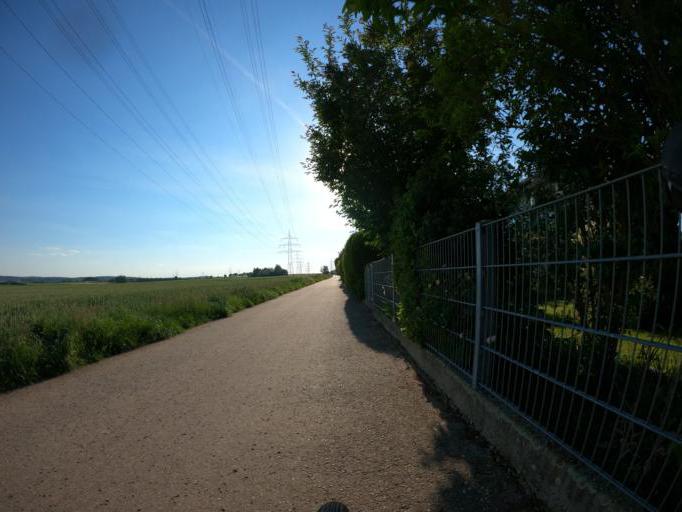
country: DE
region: Baden-Wuerttemberg
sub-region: Regierungsbezirk Stuttgart
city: Magstadt
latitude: 48.7148
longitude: 8.9618
